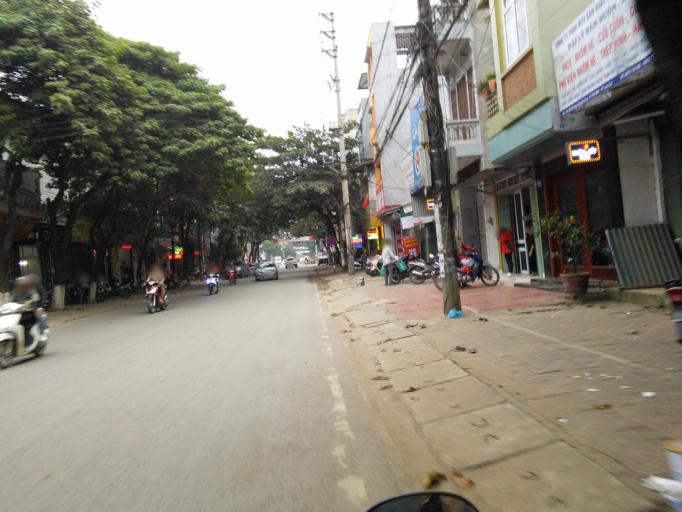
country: VN
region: Lao Cai
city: Lao Cai
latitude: 22.4932
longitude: 103.9767
